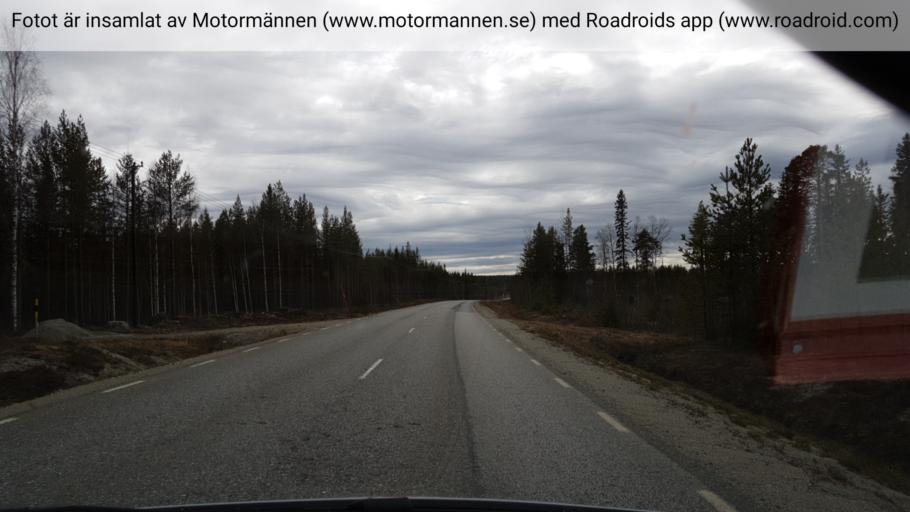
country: SE
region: Vaesterbotten
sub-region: Asele Kommun
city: Asele
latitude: 63.9294
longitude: 17.2627
